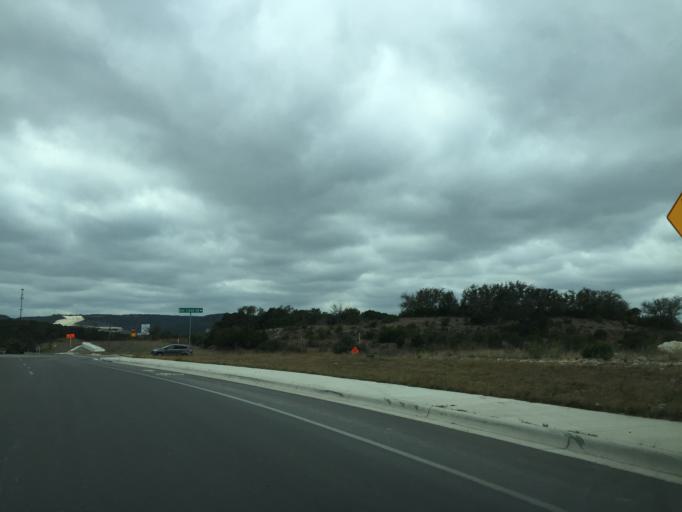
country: US
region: Texas
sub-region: Travis County
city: The Hills
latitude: 30.3436
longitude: -98.0259
